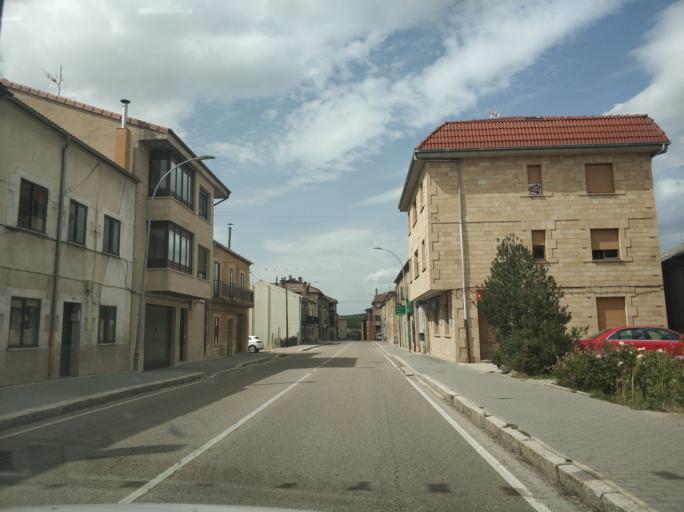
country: ES
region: Castille and Leon
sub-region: Provincia de Soria
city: Duruelo de la Sierra
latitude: 41.9535
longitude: -2.9305
